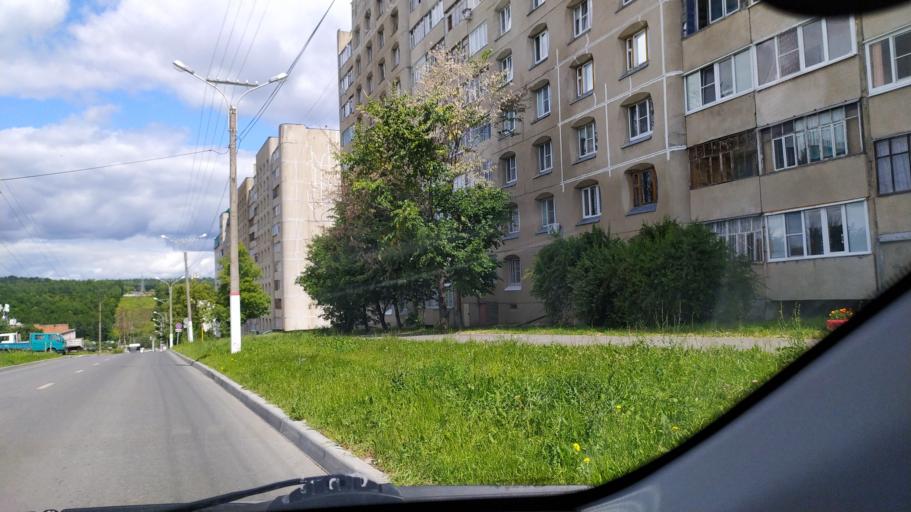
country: RU
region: Chuvashia
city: Novyye Lapsary
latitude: 56.1182
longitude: 47.1752
